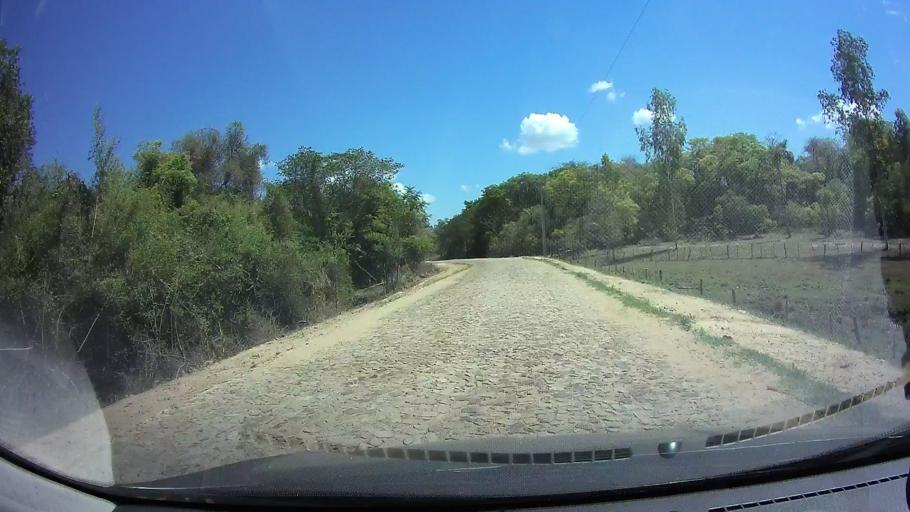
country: PY
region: Cordillera
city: Emboscada
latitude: -25.1284
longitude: -57.2684
